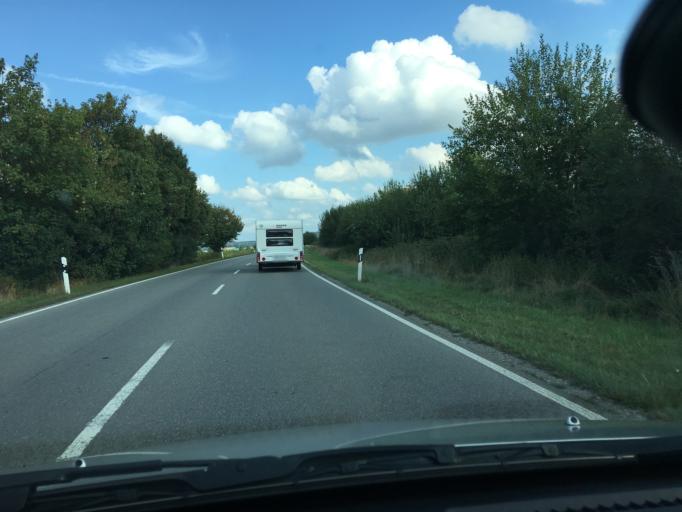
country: DE
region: Baden-Wuerttemberg
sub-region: Tuebingen Region
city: Ingoldingen
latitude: 48.0243
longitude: 9.7190
